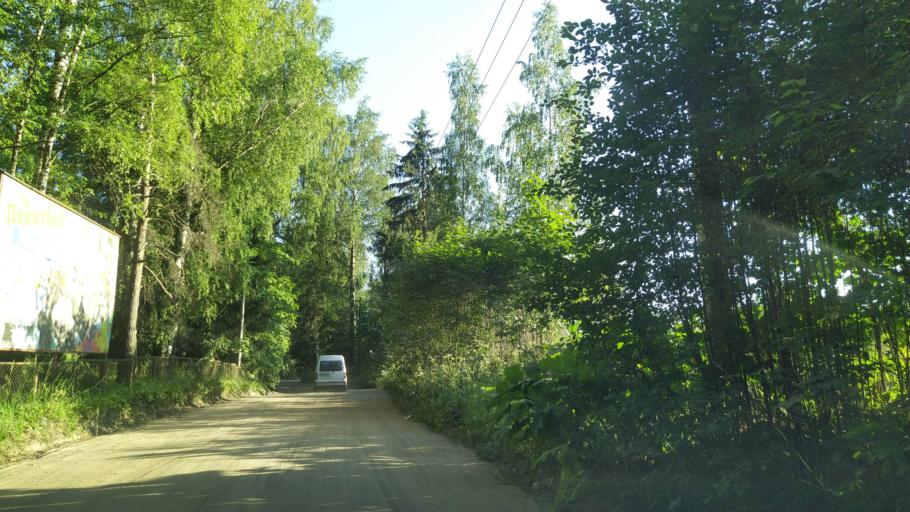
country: RU
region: Leningrad
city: Koltushi
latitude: 59.9064
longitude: 30.7360
